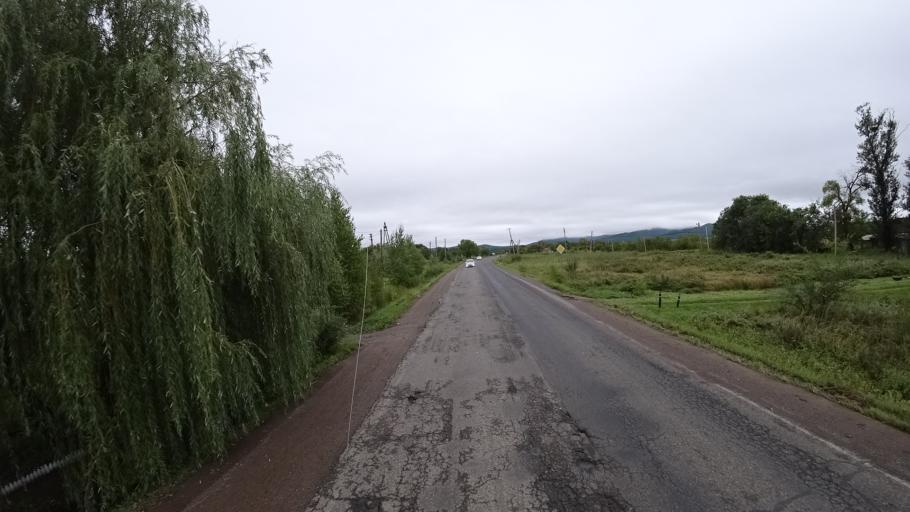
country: RU
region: Primorskiy
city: Monastyrishche
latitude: 44.1971
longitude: 132.4786
